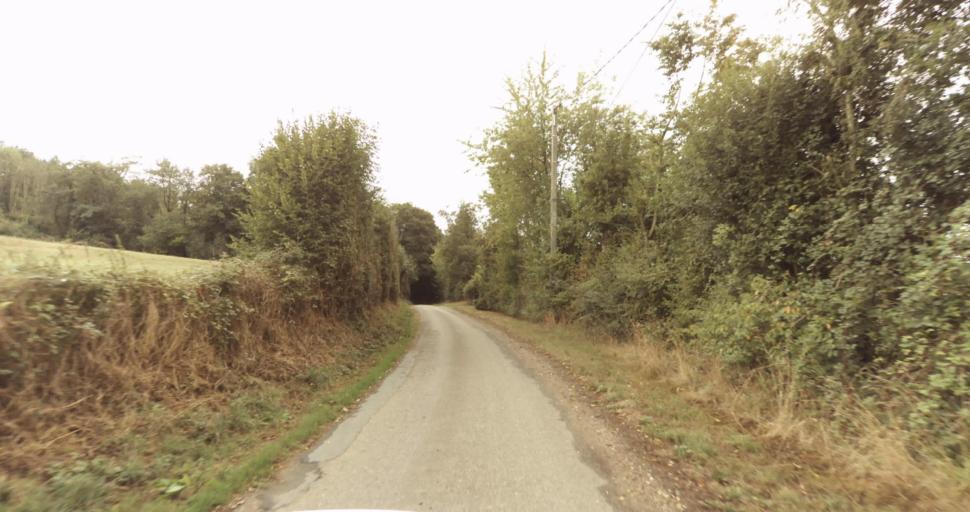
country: FR
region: Lower Normandy
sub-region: Departement de l'Orne
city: Trun
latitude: 48.9205
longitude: 0.0951
